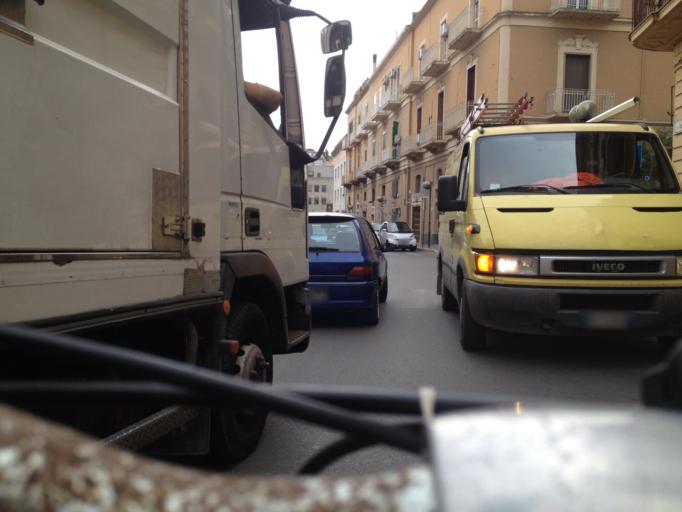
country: IT
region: Basilicate
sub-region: Provincia di Matera
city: Matera
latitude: 40.6674
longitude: 16.6045
